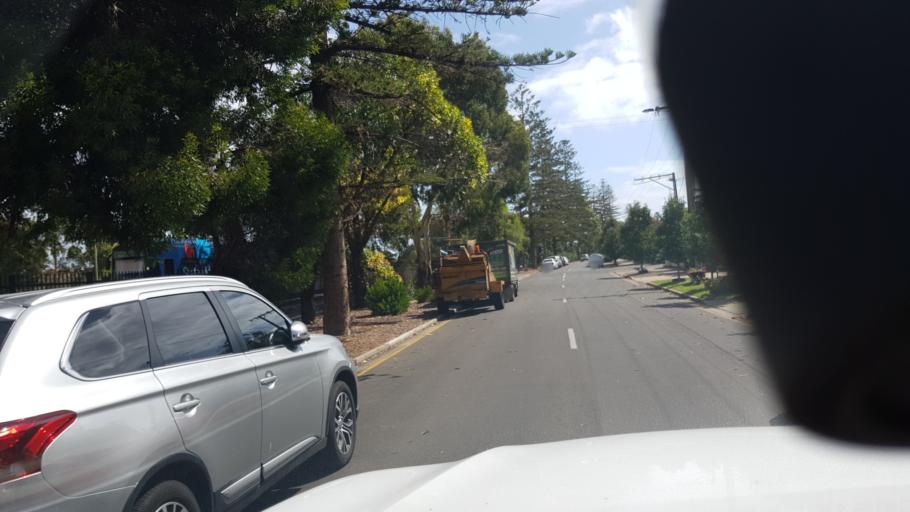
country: AU
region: South Australia
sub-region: Holdfast Bay
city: Glenelg East
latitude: -34.9784
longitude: 138.5323
